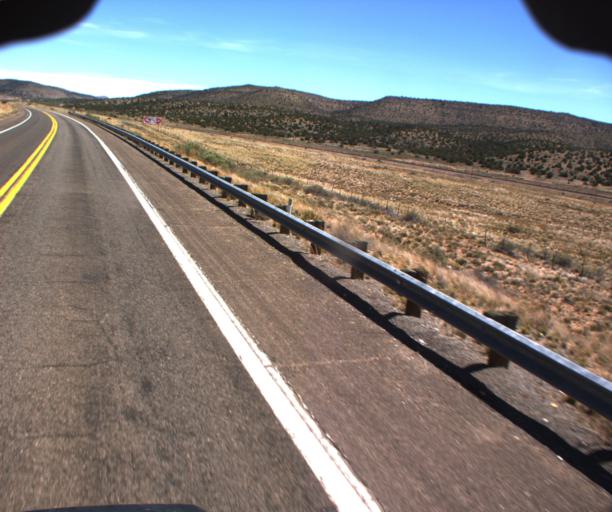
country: US
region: Arizona
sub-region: Mohave County
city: Peach Springs
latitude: 35.5218
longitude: -113.4523
